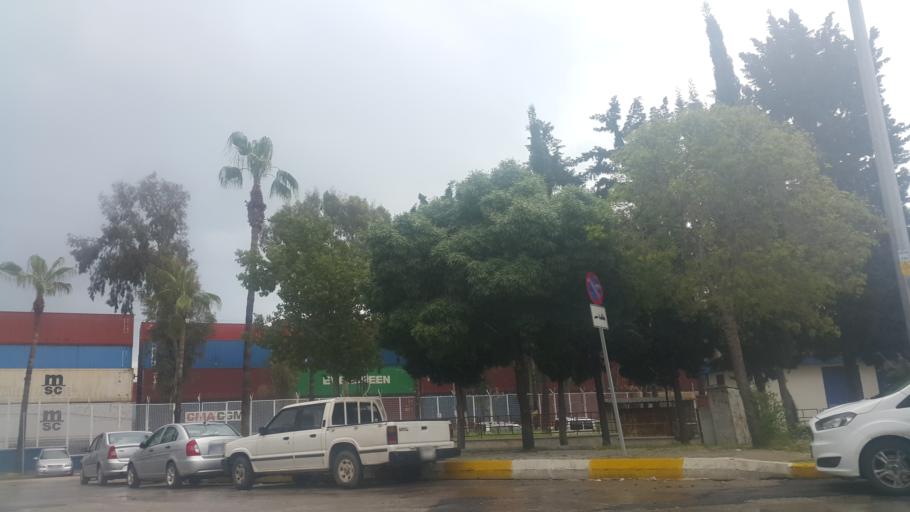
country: TR
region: Mersin
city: Mercin
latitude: 36.8020
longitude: 34.6378
